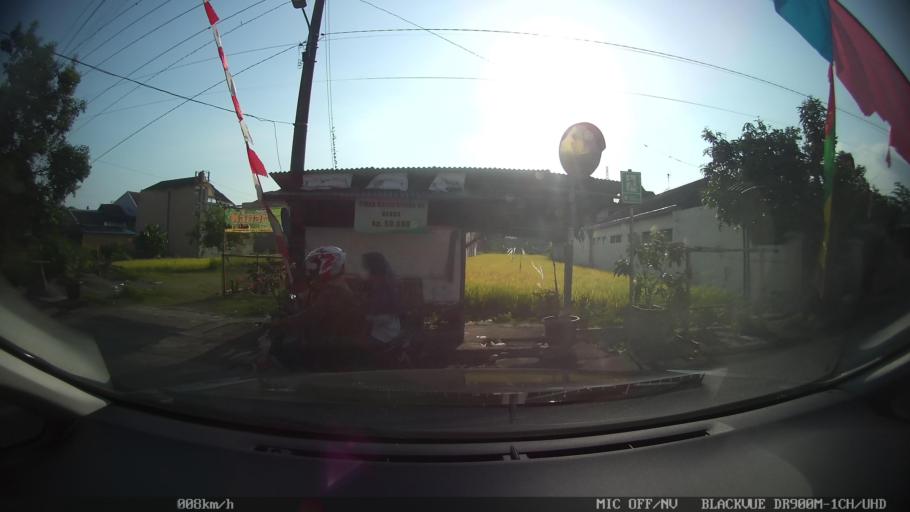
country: ID
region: Daerah Istimewa Yogyakarta
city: Yogyakarta
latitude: -7.8247
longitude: 110.3881
